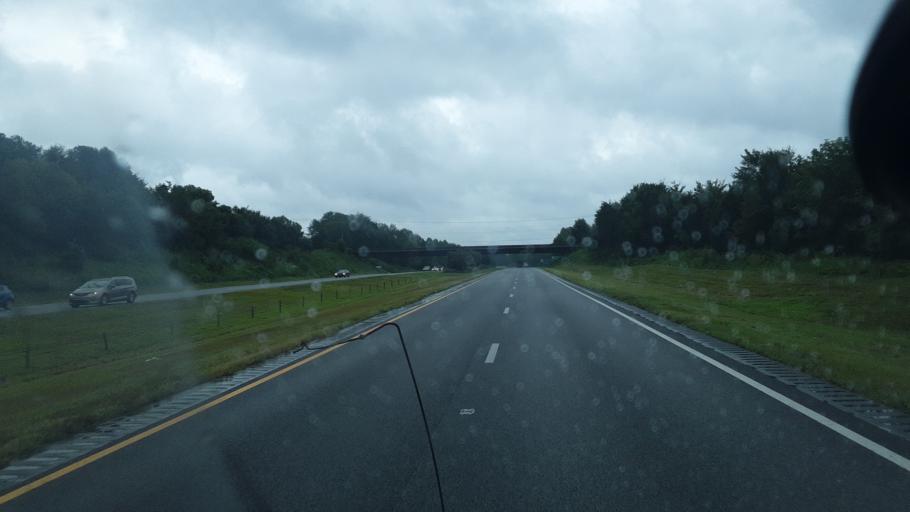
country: US
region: North Carolina
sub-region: Guilford County
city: High Point
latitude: 36.0179
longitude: -80.0450
